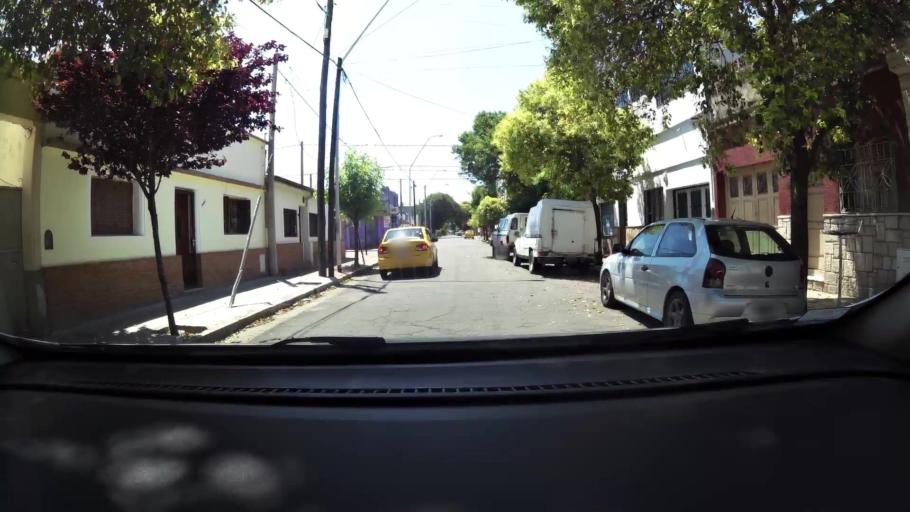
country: AR
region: Cordoba
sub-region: Departamento de Capital
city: Cordoba
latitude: -31.3815
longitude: -64.2025
